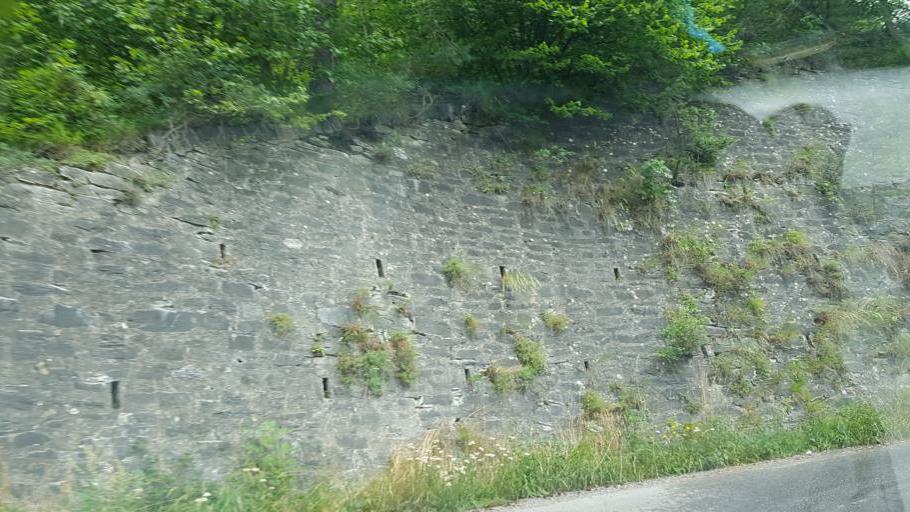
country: IT
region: Piedmont
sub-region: Provincia di Cuneo
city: Stroppo
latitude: 44.5136
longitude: 7.1259
